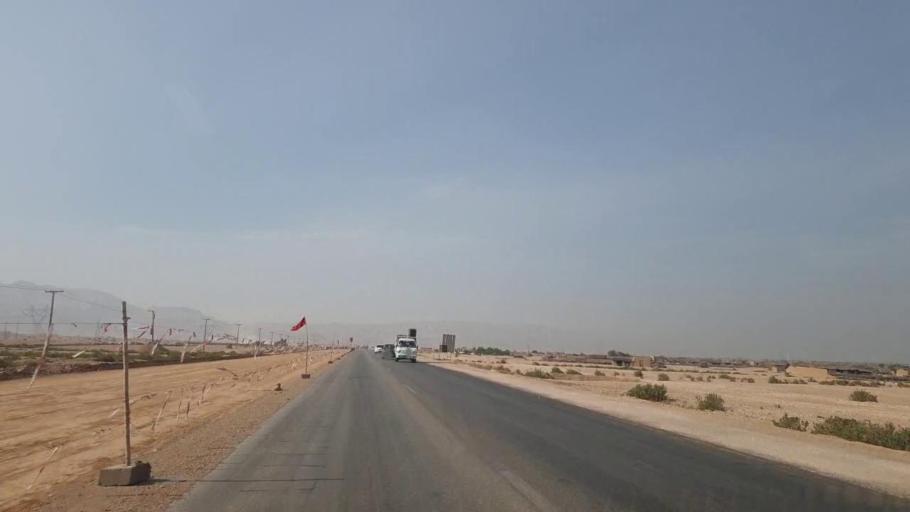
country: PK
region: Sindh
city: Sehwan
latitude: 26.1985
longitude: 67.9415
